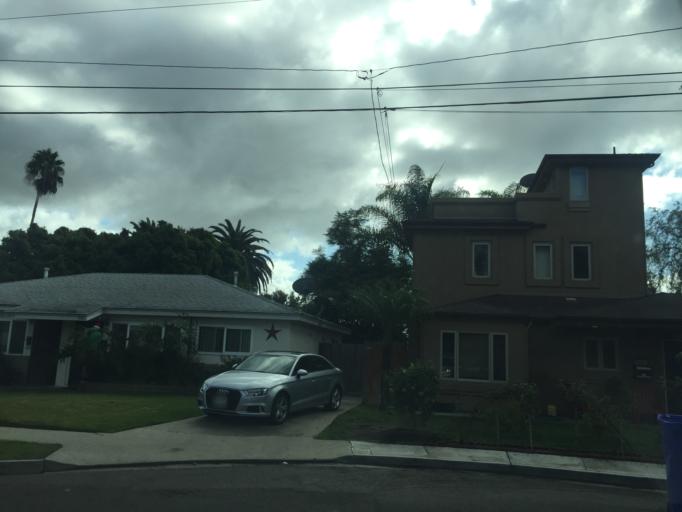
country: US
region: California
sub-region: San Diego County
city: La Jolla
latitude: 32.8043
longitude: -117.2226
